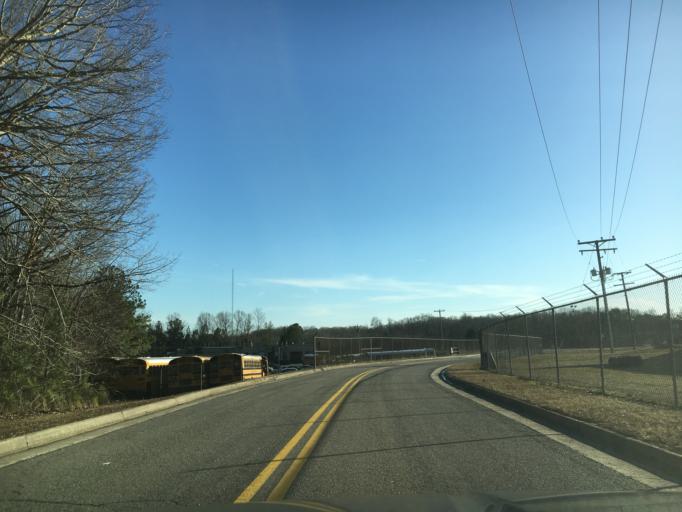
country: US
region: Virginia
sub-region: Halifax County
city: South Boston
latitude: 36.7274
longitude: -78.9144
